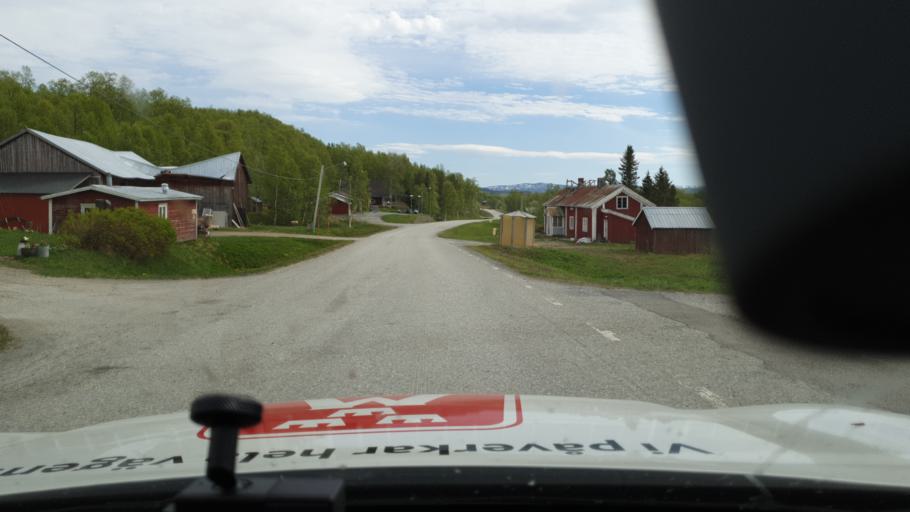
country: NO
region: Nordland
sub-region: Rana
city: Mo i Rana
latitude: 65.7532
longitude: 15.1640
